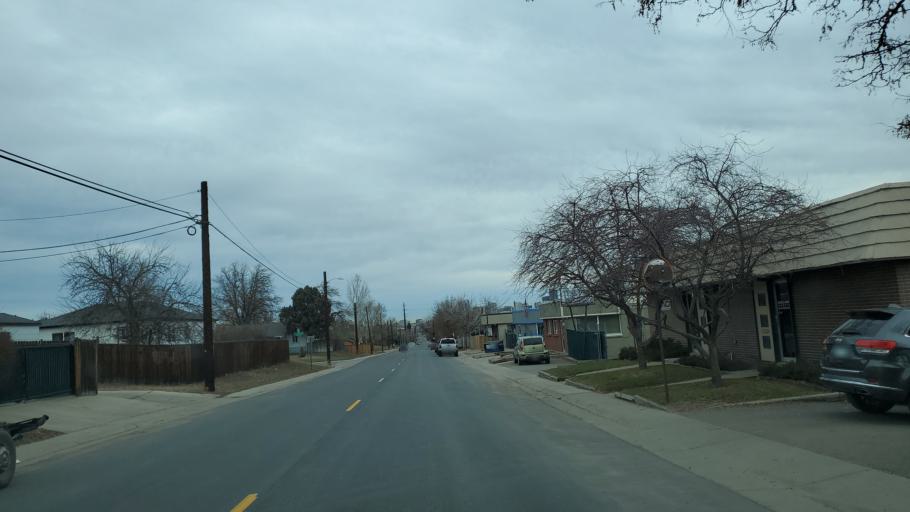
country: US
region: Colorado
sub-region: Denver County
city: Denver
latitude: 39.7000
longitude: -105.0015
